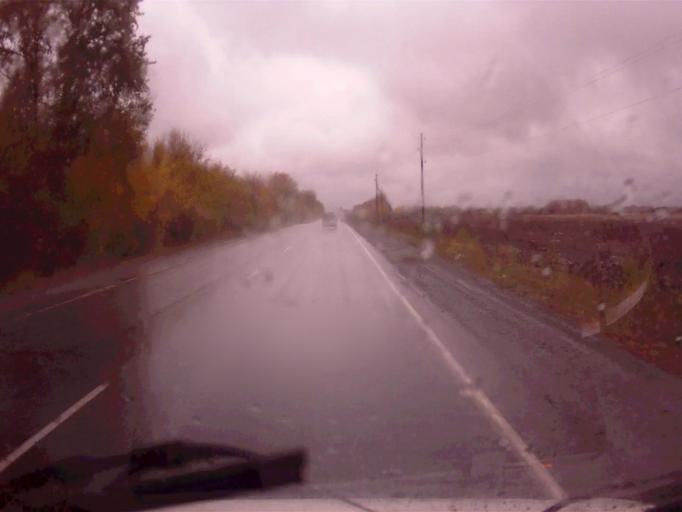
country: RU
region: Chelyabinsk
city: Argayash
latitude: 55.4318
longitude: 60.9871
